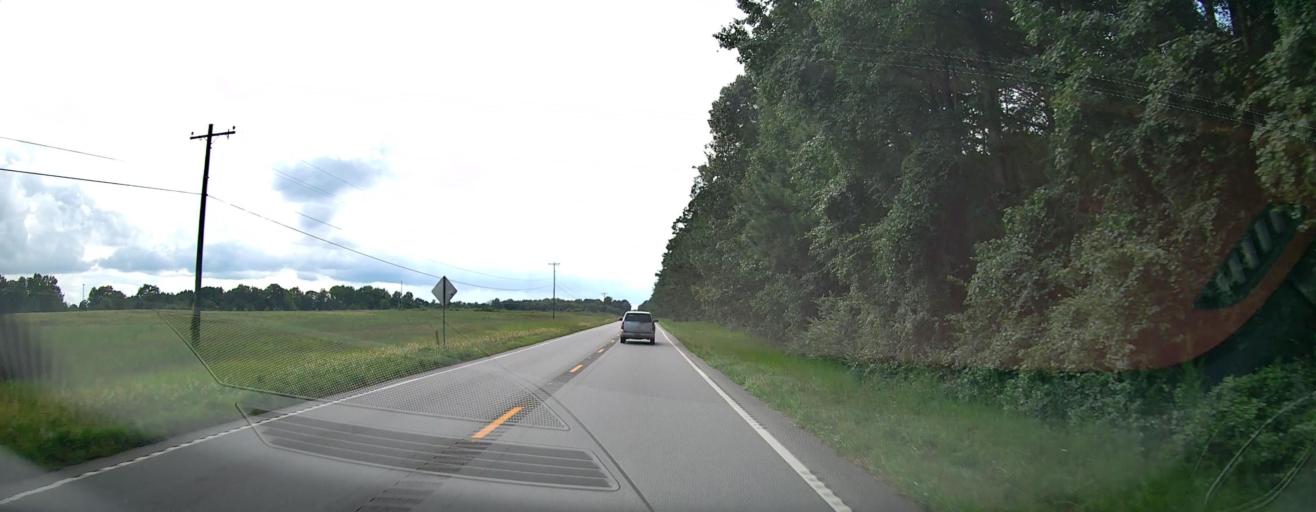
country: US
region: Georgia
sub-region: Meriwether County
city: Manchester
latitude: 32.9851
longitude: -84.5512
